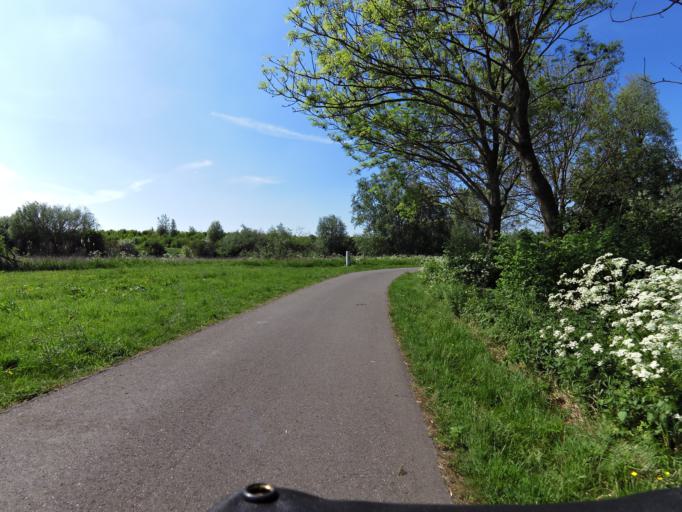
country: NL
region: South Holland
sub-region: Gemeente Barendrecht
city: Barendrecht
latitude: 51.8343
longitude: 4.5194
